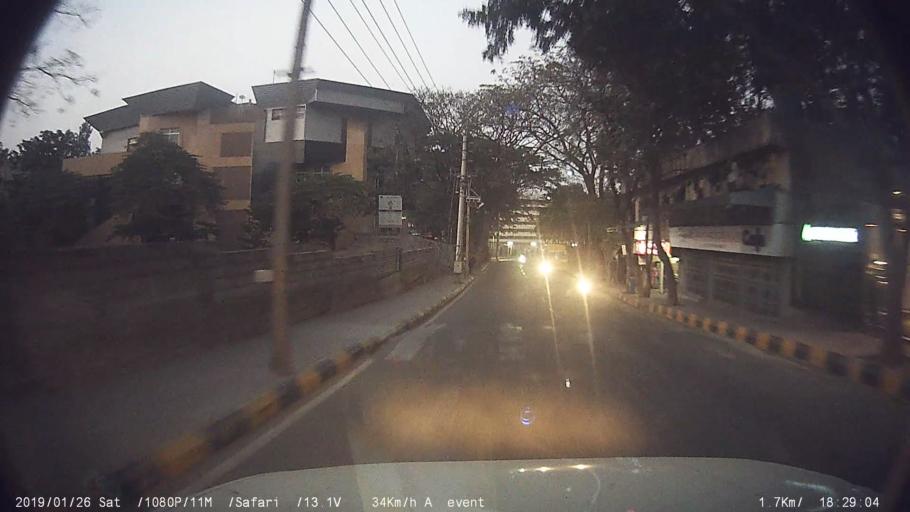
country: IN
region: Karnataka
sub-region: Bangalore Urban
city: Anekal
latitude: 12.8483
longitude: 77.6625
